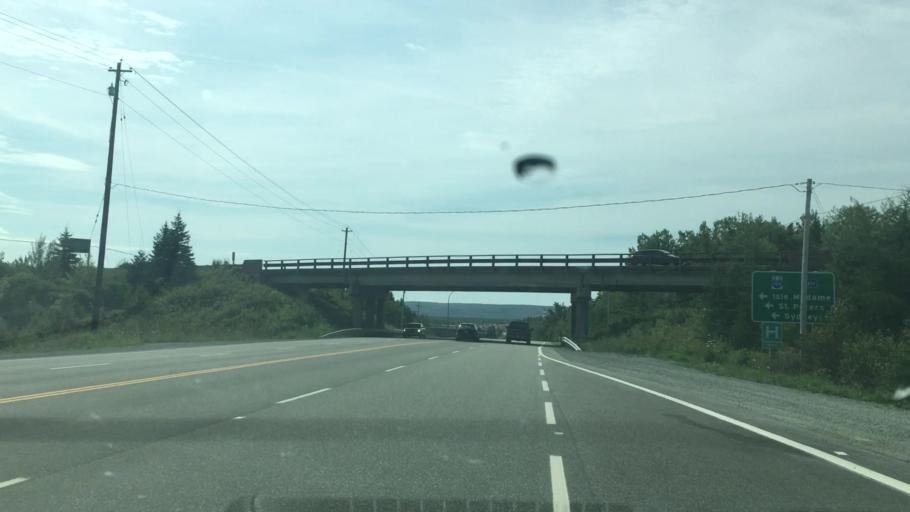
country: CA
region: Nova Scotia
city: Port Hawkesbury
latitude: 45.6257
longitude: -61.3324
